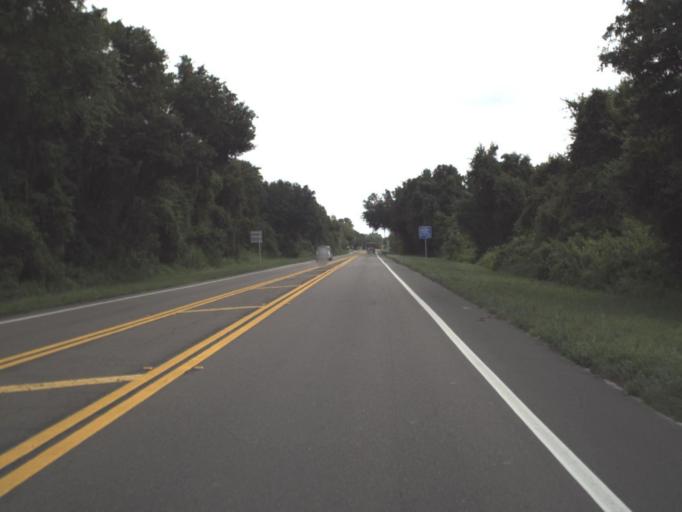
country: US
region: Florida
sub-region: Pasco County
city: Crystal Springs
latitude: 28.1734
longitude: -82.1564
